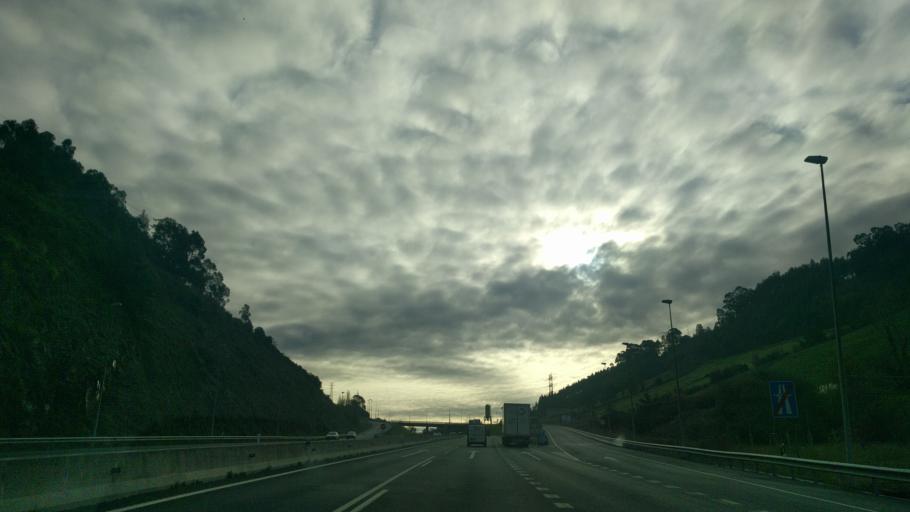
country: ES
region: Basque Country
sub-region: Bizkaia
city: San Julian de Muskiz
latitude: 43.3461
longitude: -3.1603
